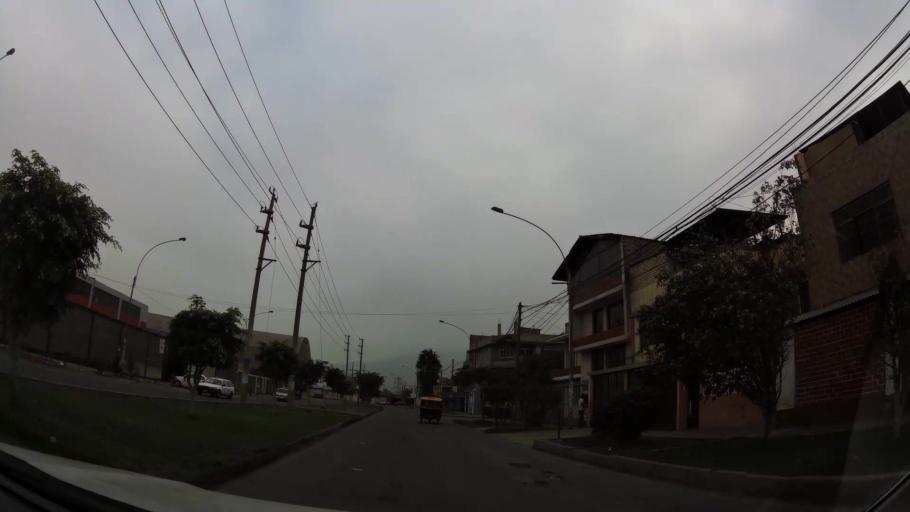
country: PE
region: Lima
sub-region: Lima
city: Independencia
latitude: -11.9762
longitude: -77.0042
